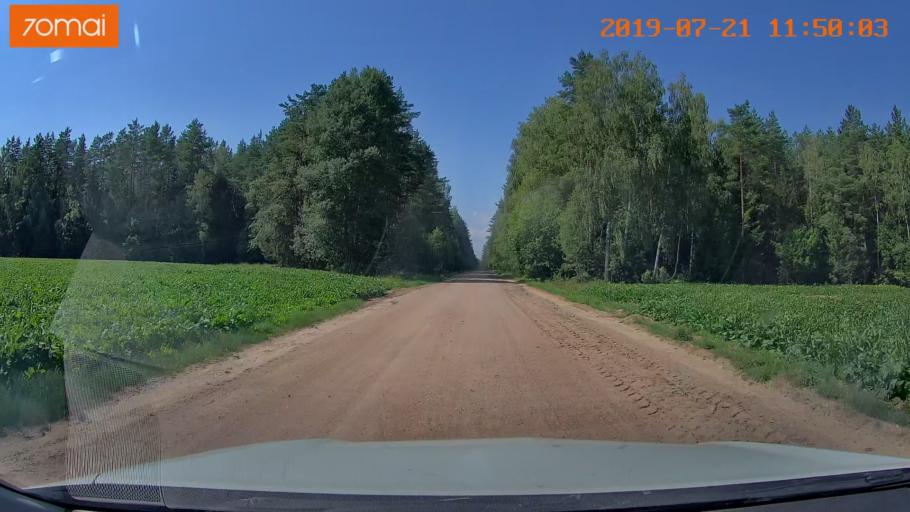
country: BY
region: Grodnenskaya
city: Lyubcha
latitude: 53.8892
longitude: 26.0314
